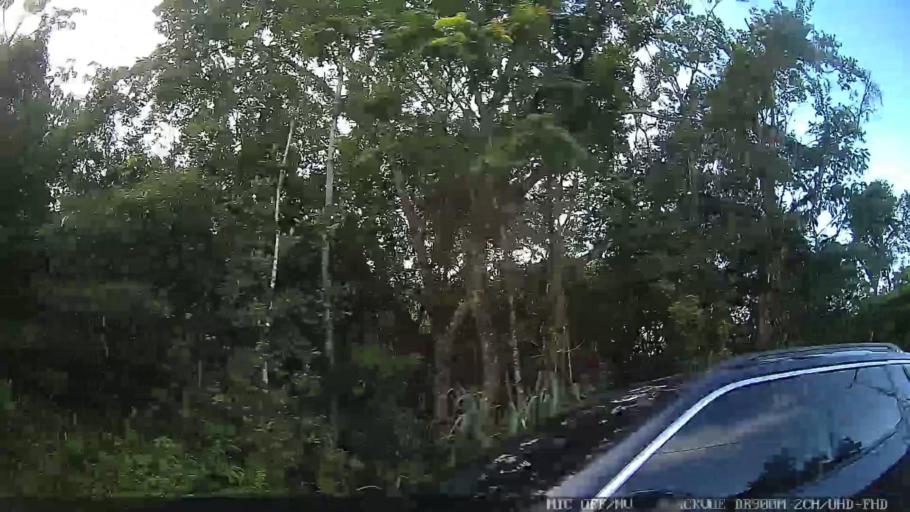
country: BR
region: Sao Paulo
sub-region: Itanhaem
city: Itanhaem
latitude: -24.2163
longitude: -46.9154
